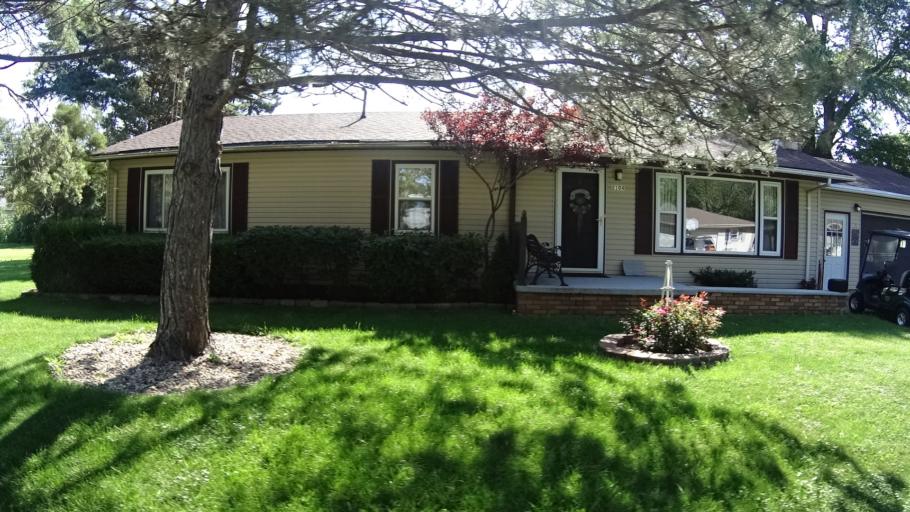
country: US
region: Ohio
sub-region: Erie County
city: Sandusky
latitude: 41.4678
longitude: -82.8206
